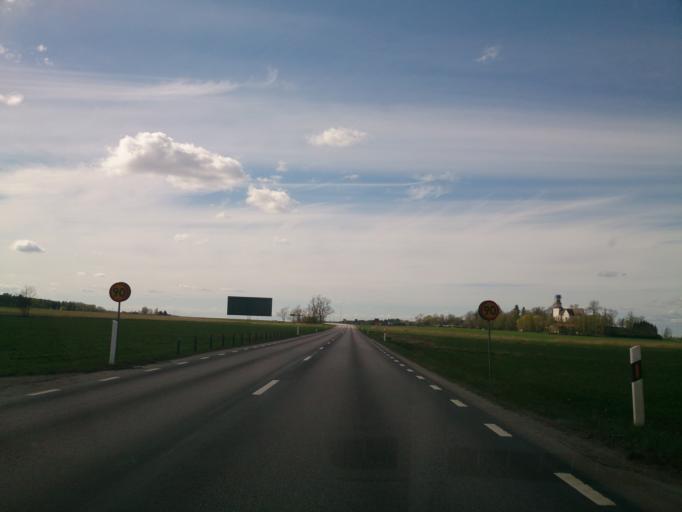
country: SE
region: OEstergoetland
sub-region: Linkopings Kommun
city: Linghem
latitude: 58.3991
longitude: 15.7605
